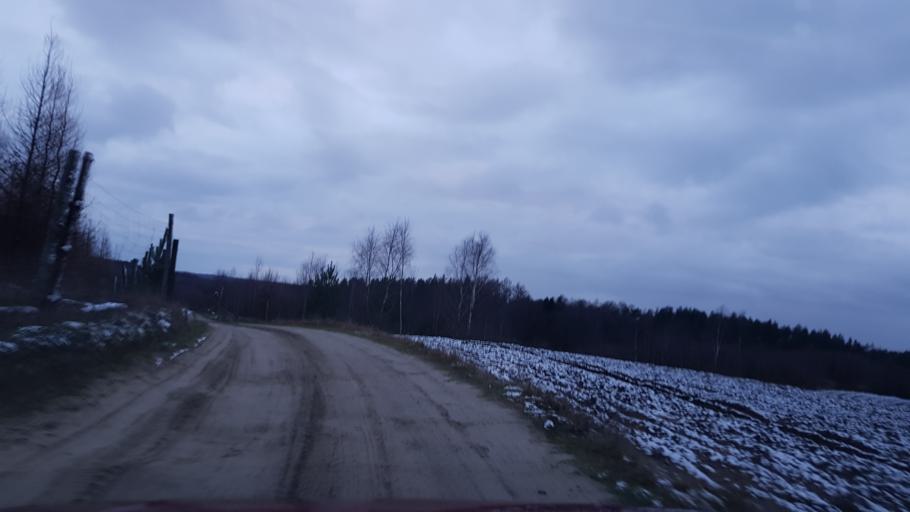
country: PL
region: Pomeranian Voivodeship
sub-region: Powiat bytowski
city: Tuchomie
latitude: 54.1472
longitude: 17.3030
